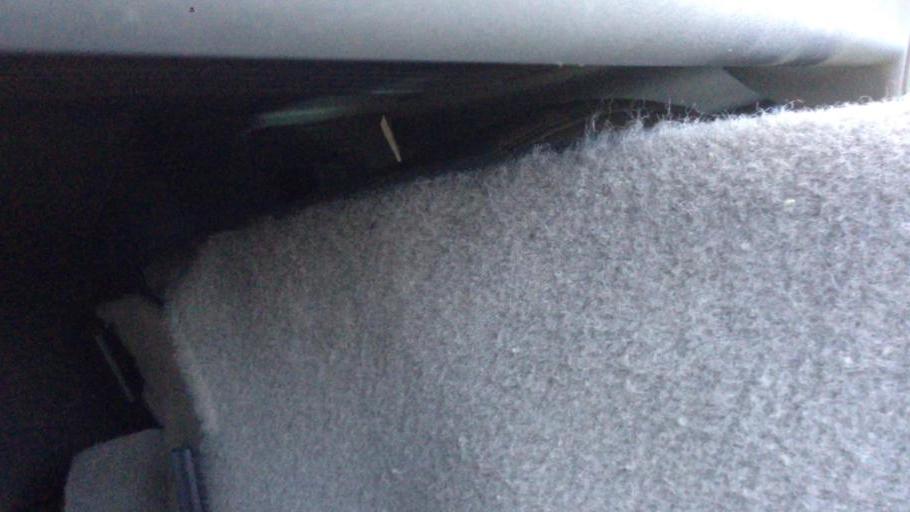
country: US
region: New York
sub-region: Dutchess County
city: Tivoli
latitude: 42.1097
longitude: -73.8171
